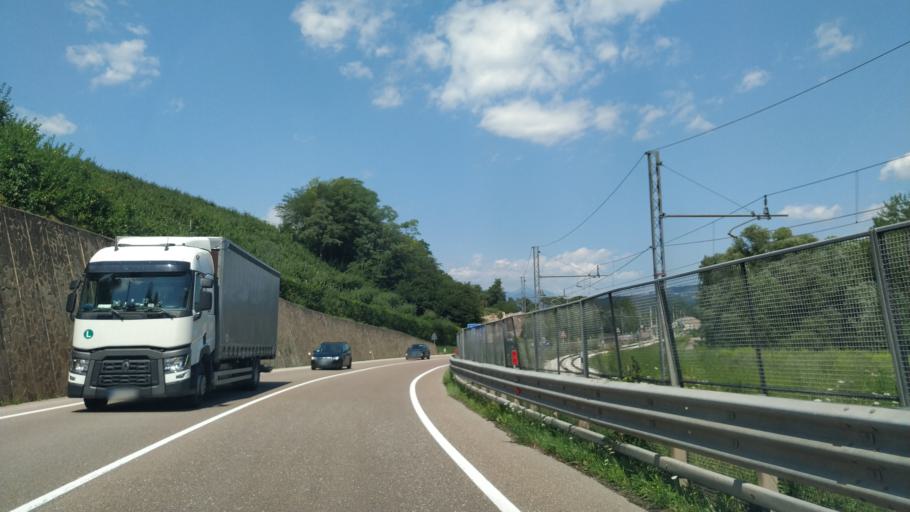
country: IT
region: Trentino-Alto Adige
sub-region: Provincia di Trento
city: Campodenno
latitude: 46.2455
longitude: 11.0567
